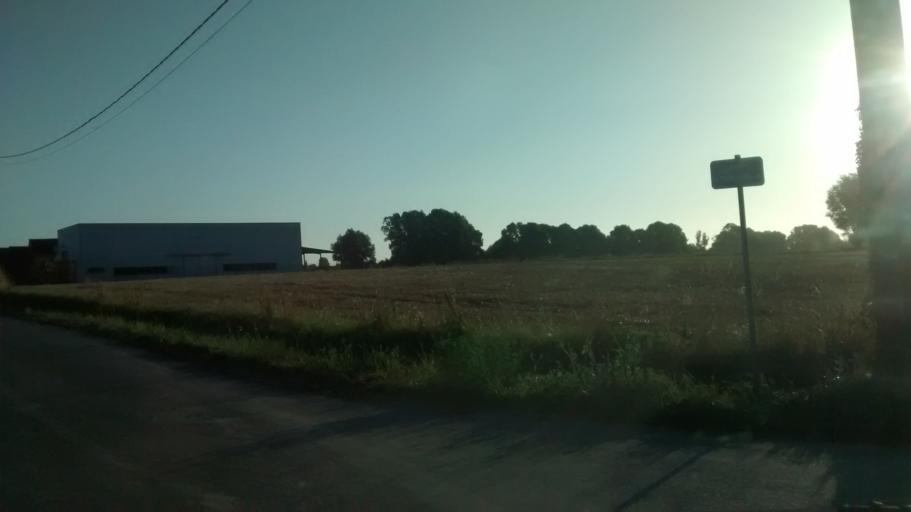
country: FR
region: Brittany
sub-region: Departement d'Ille-et-Vilaine
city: La Fresnais
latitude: 48.5804
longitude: -1.8629
